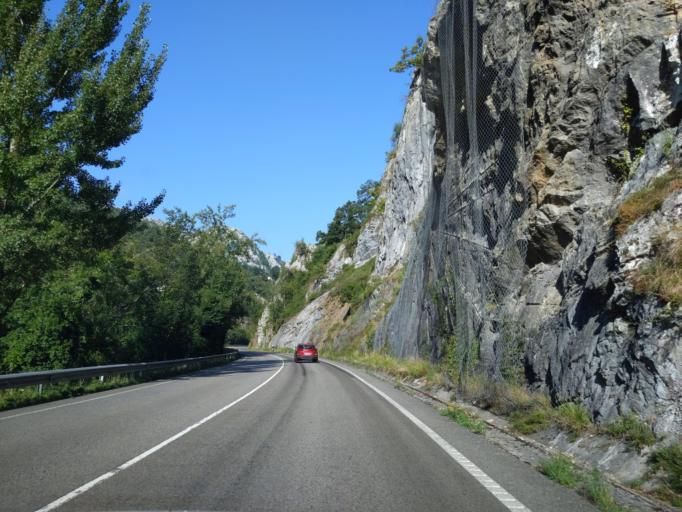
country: ES
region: Asturias
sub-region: Province of Asturias
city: Pola de Laviana
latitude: 43.2321
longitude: -5.4898
